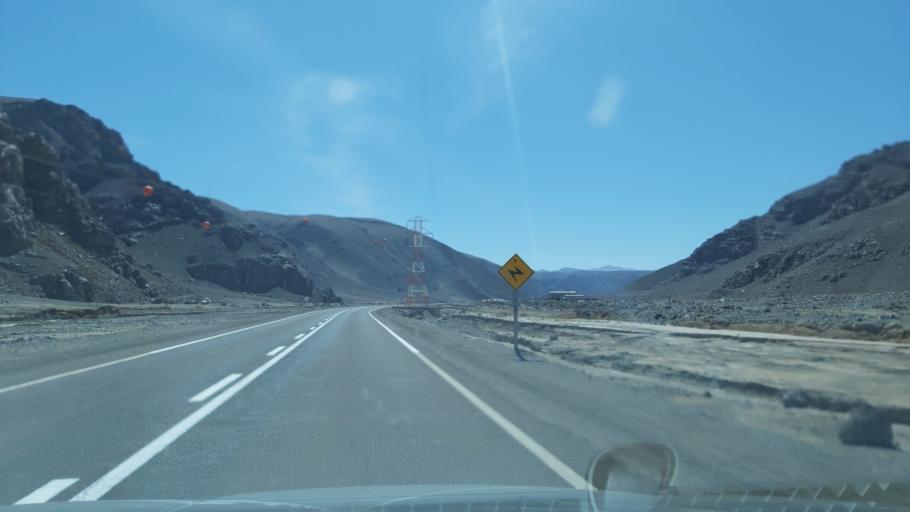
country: CL
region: Atacama
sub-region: Provincia de Chanaral
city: Diego de Almagro
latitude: -26.3372
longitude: -69.8327
